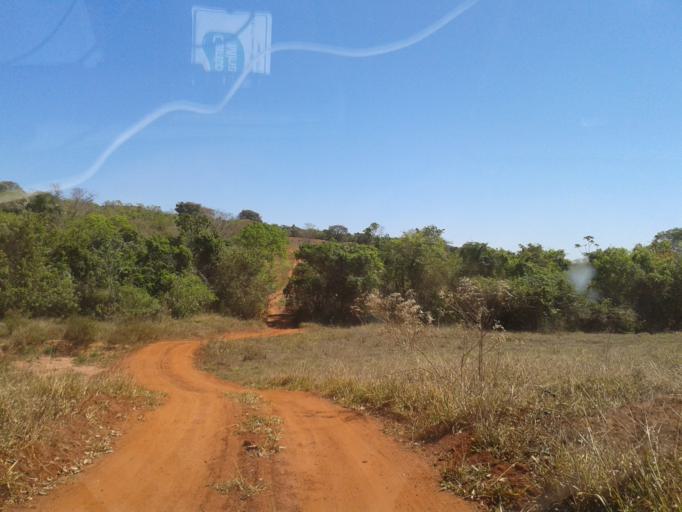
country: BR
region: Minas Gerais
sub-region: Ituiutaba
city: Ituiutaba
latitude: -19.0877
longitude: -49.2597
